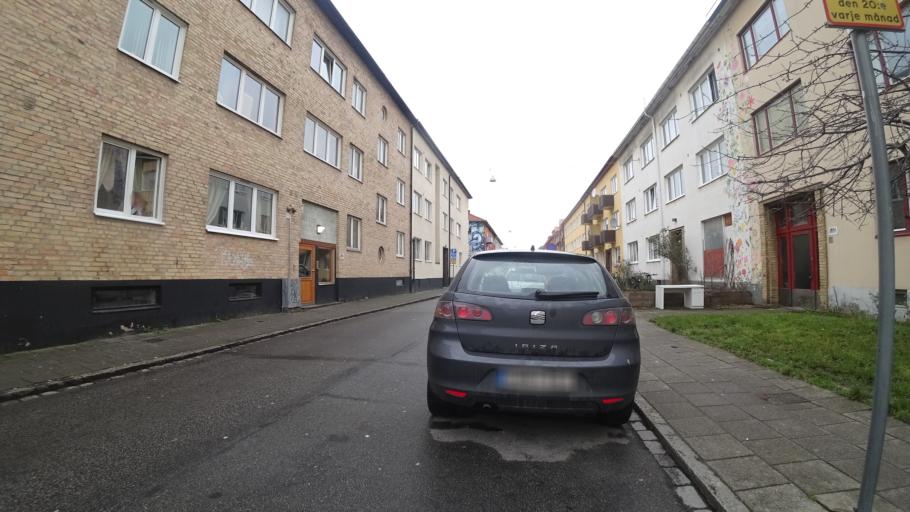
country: SE
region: Skane
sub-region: Malmo
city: Malmoe
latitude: 55.5829
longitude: 13.0173
